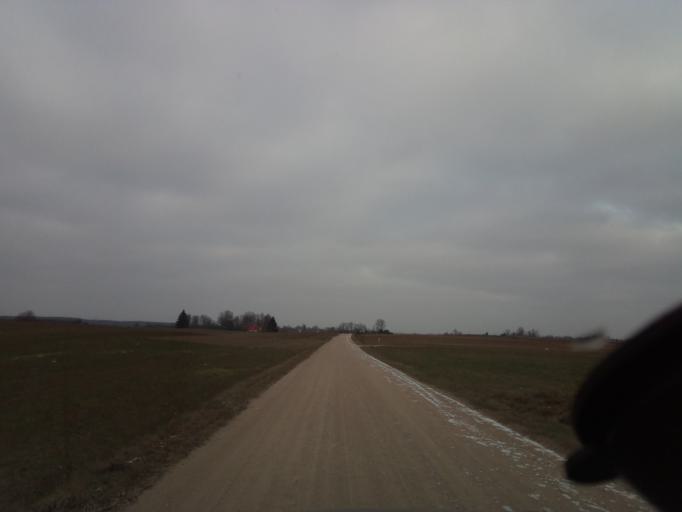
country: LT
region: Alytaus apskritis
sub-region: Alytaus rajonas
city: Daugai
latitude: 54.3768
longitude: 24.4391
